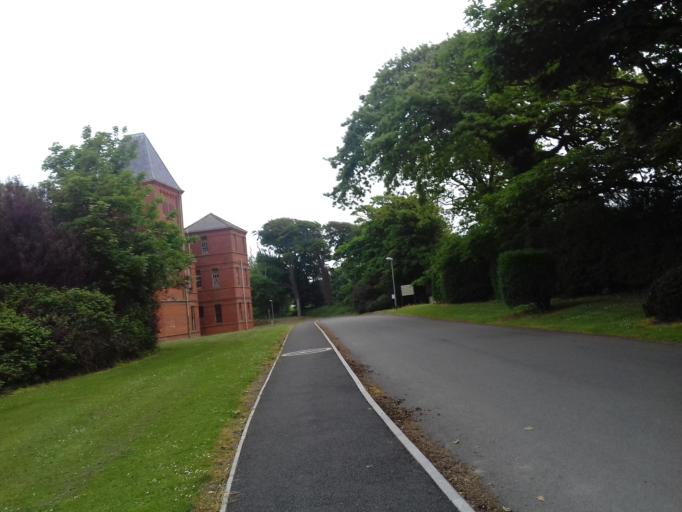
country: IE
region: Leinster
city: Portraine
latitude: 53.4859
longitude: -6.1093
